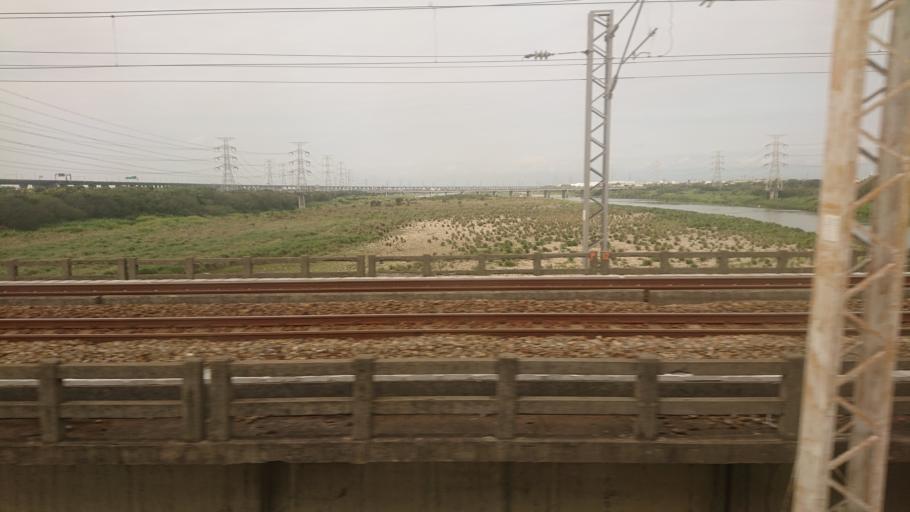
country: TW
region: Taiwan
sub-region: Changhua
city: Chang-hua
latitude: 24.1071
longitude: 120.5772
